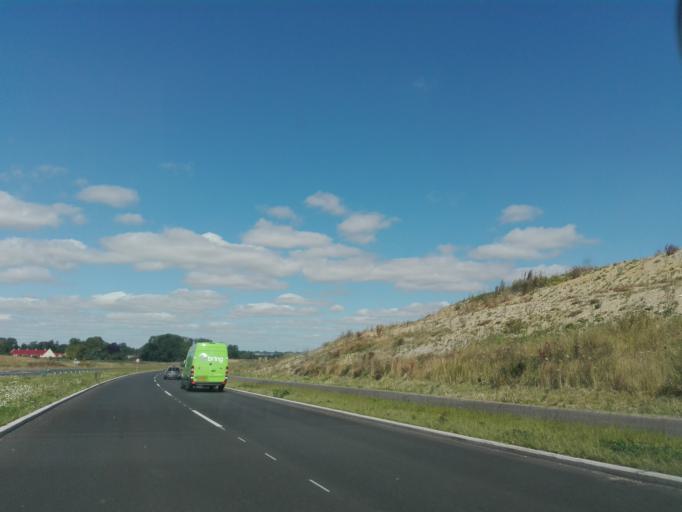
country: DK
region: Central Jutland
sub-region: Arhus Kommune
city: Arhus
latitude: 56.1854
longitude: 10.1651
